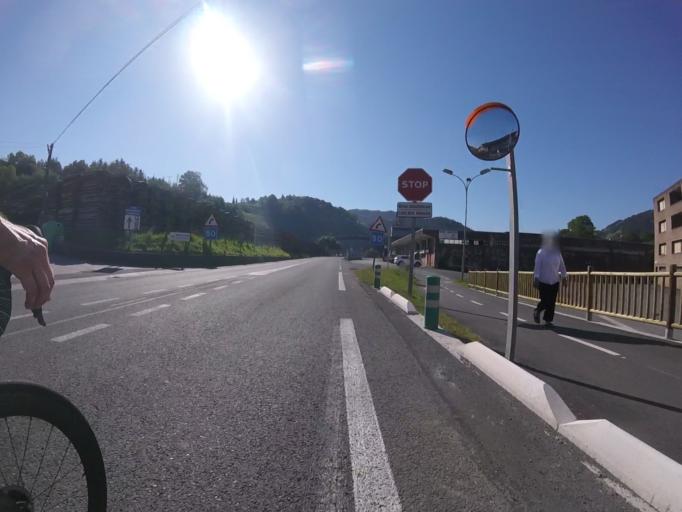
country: ES
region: Basque Country
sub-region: Provincia de Guipuzcoa
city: Azpeitia
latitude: 43.1642
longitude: -2.2479
